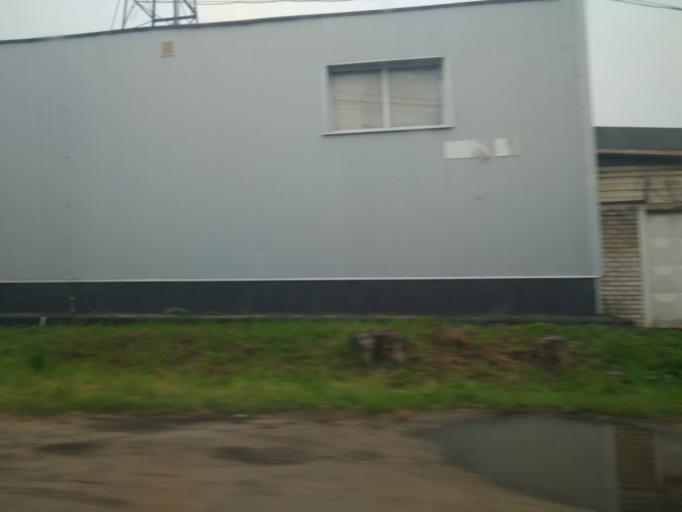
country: RU
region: Moskovskaya
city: Zhukovskiy
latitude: 55.5803
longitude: 38.1086
